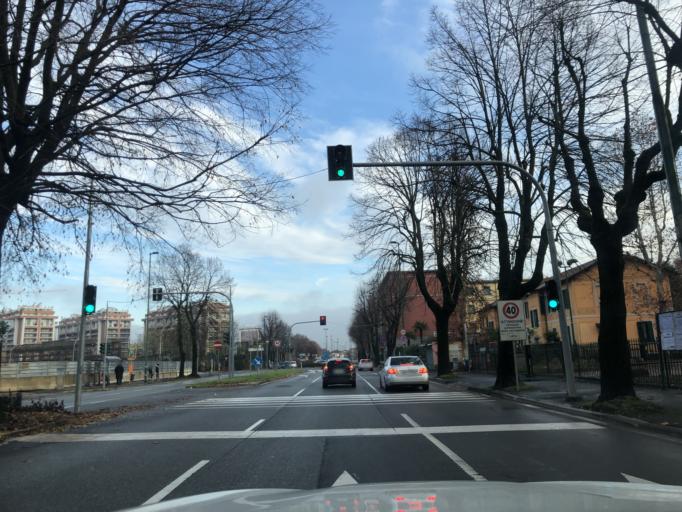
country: IT
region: Lombardy
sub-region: Citta metropolitana di Milano
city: Sesto San Giovanni
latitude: 45.5442
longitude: 9.2532
